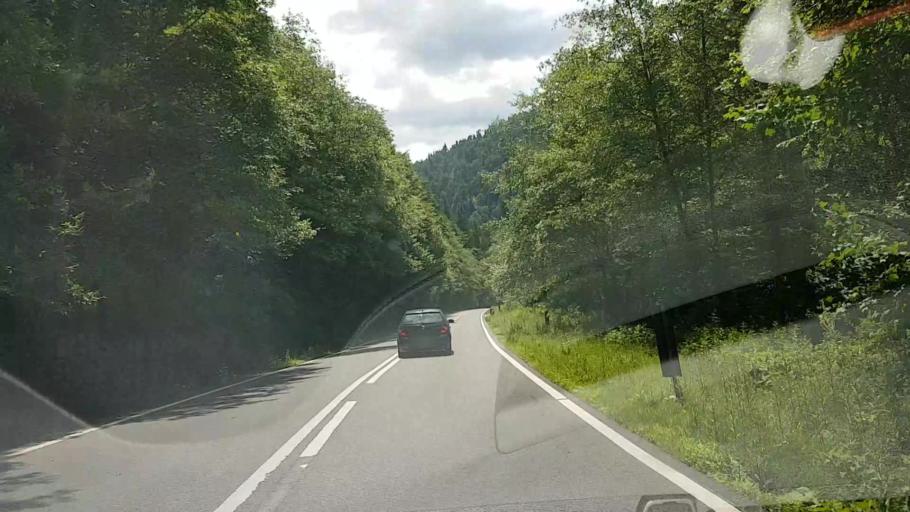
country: RO
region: Suceava
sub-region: Comuna Brosteni
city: Brosteni
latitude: 47.2797
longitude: 25.6502
